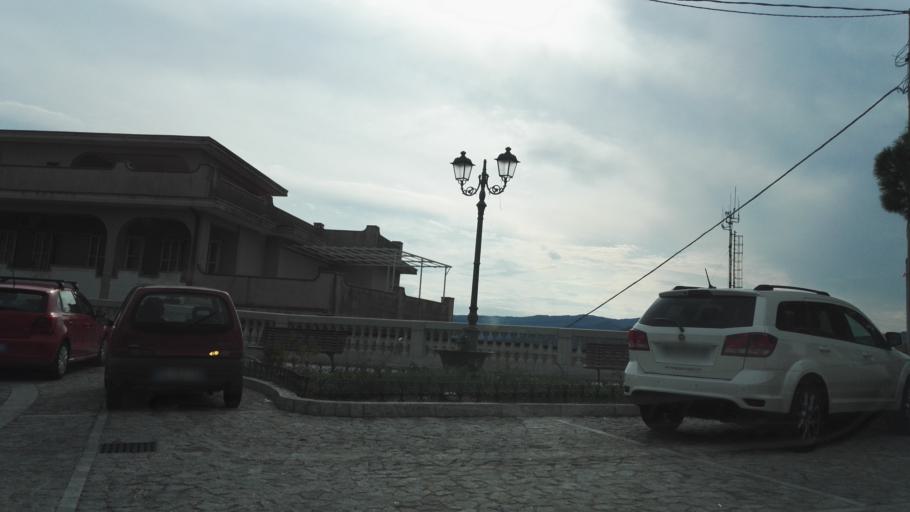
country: IT
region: Calabria
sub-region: Provincia di Reggio Calabria
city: Stignano
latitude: 38.4189
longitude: 16.4707
